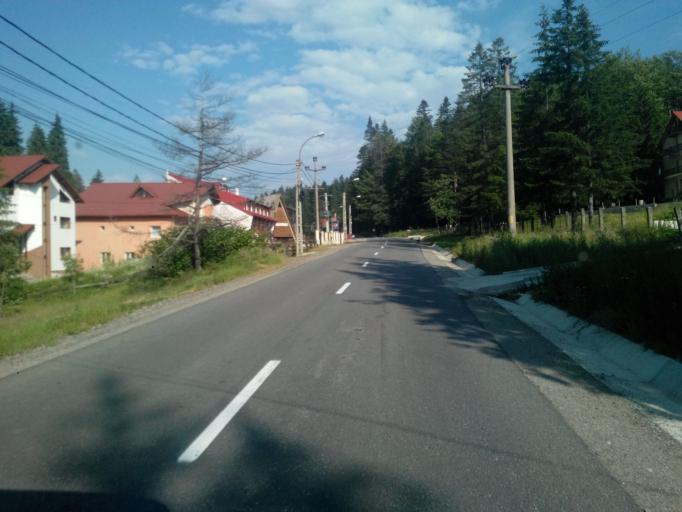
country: RO
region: Brasov
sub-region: Oras Predeal
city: Predeal
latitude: 45.4967
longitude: 25.5359
